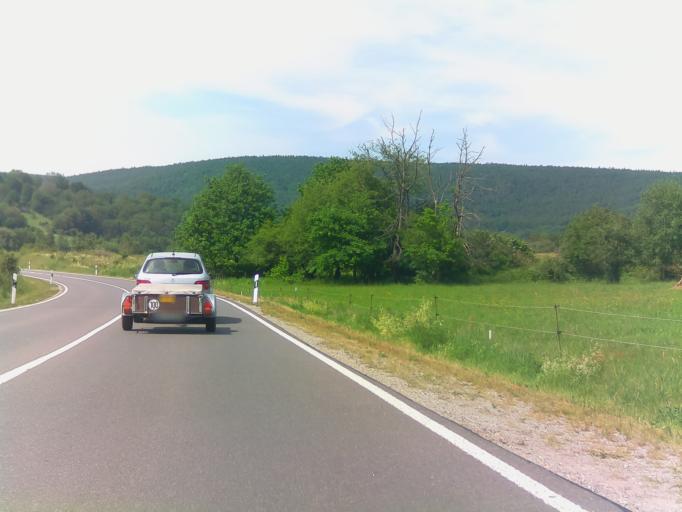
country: DE
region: Bavaria
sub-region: Regierungsbezirk Unterfranken
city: Faulbach
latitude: 49.7844
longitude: 9.4525
